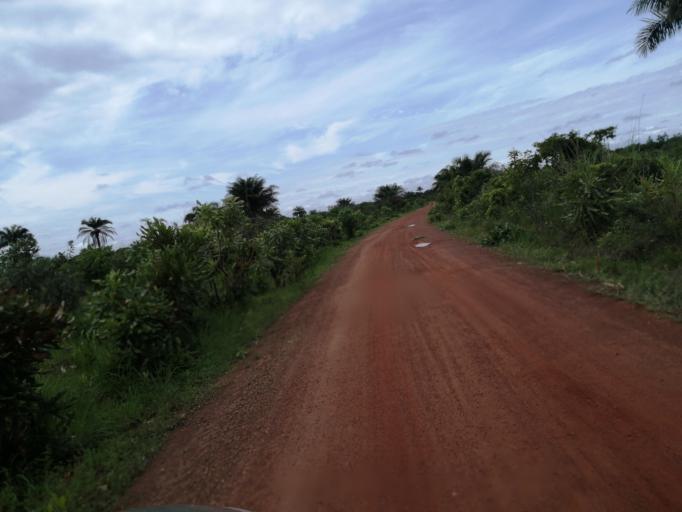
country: SL
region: Northern Province
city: Port Loko
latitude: 8.7732
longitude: -12.9153
